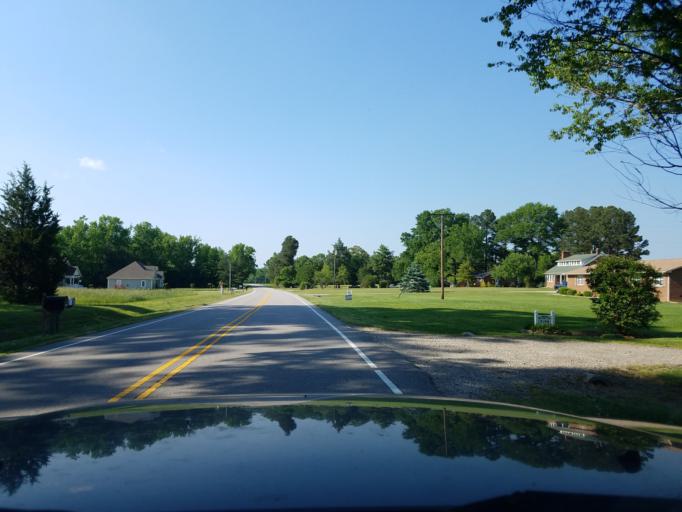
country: US
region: North Carolina
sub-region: Vance County
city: Henderson
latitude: 36.3980
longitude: -78.3683
